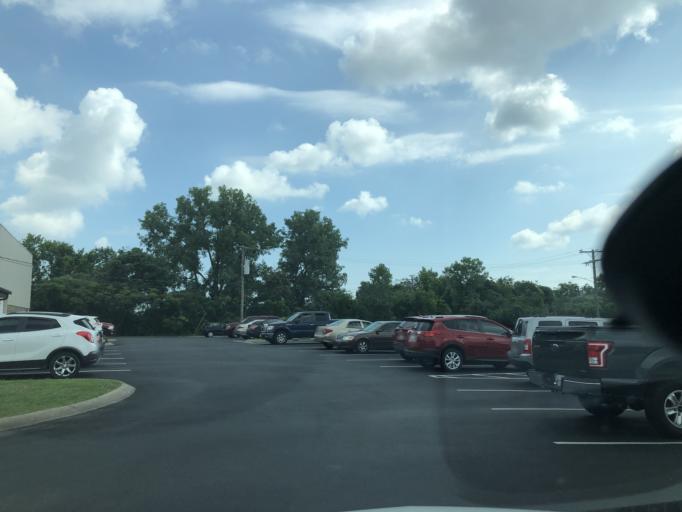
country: US
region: Tennessee
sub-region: Rutherford County
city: La Vergne
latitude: 36.0153
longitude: -86.6082
